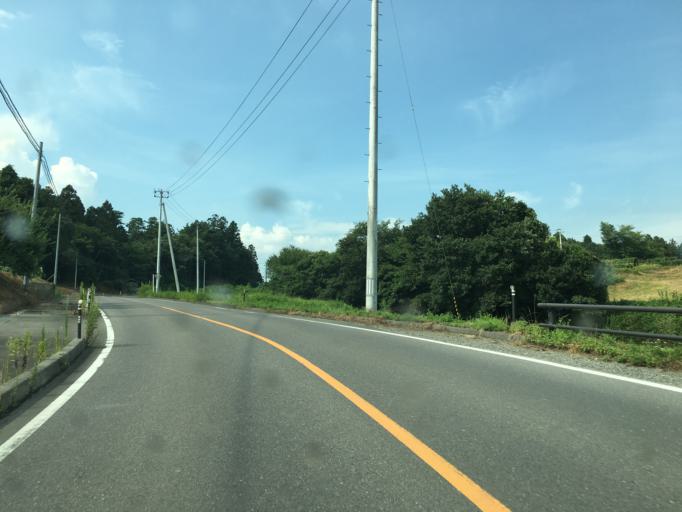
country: JP
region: Fukushima
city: Koriyama
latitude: 37.3565
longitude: 140.4170
